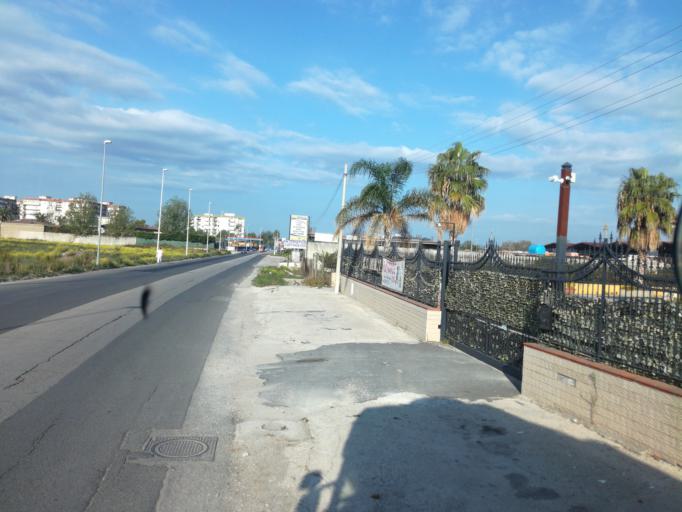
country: IT
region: Campania
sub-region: Provincia di Napoli
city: Giugliano in Campania
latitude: 40.9390
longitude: 14.1814
